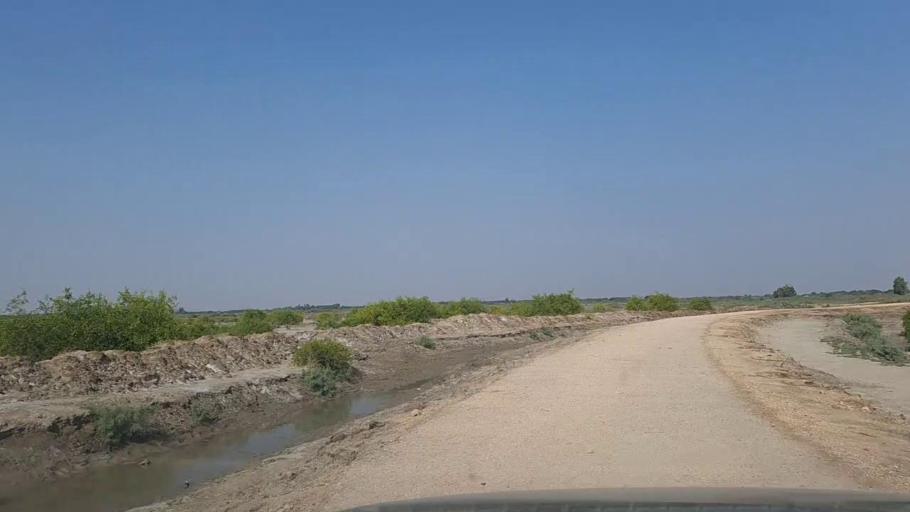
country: PK
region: Sindh
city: Mirpur Sakro
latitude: 24.5074
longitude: 67.7800
